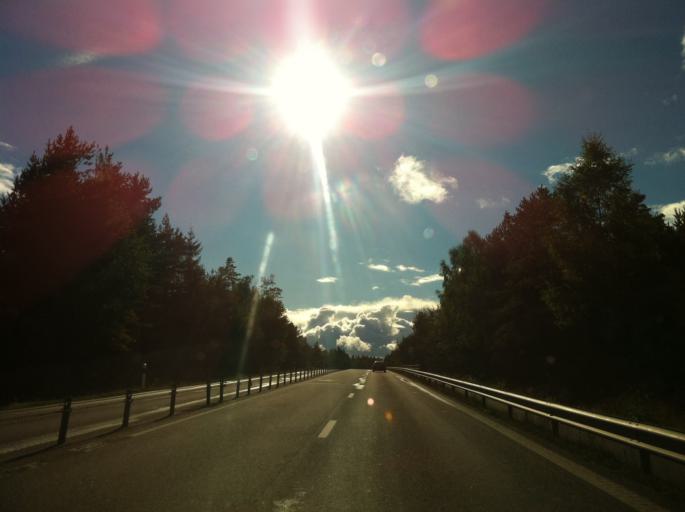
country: SE
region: Skane
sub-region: Hassleholms Kommun
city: Sosdala
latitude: 56.1623
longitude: 13.5751
